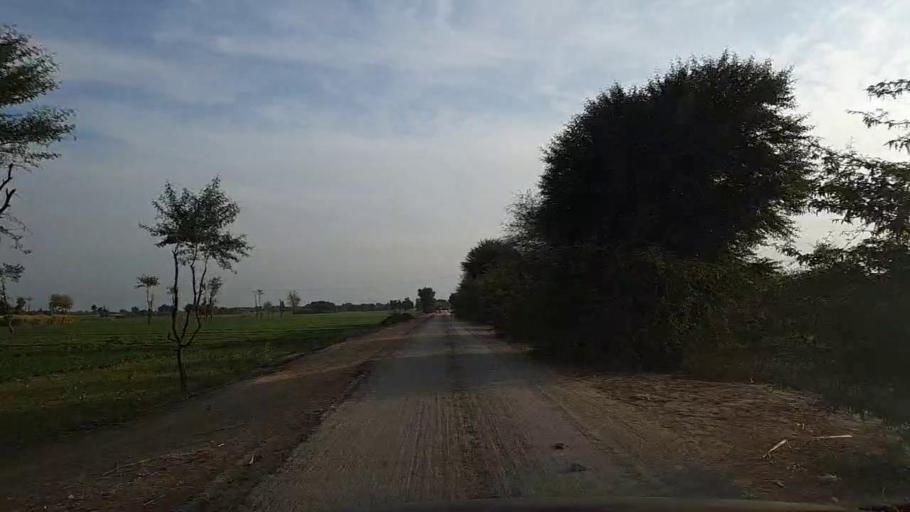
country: PK
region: Sindh
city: Jam Sahib
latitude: 26.4350
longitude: 68.5715
